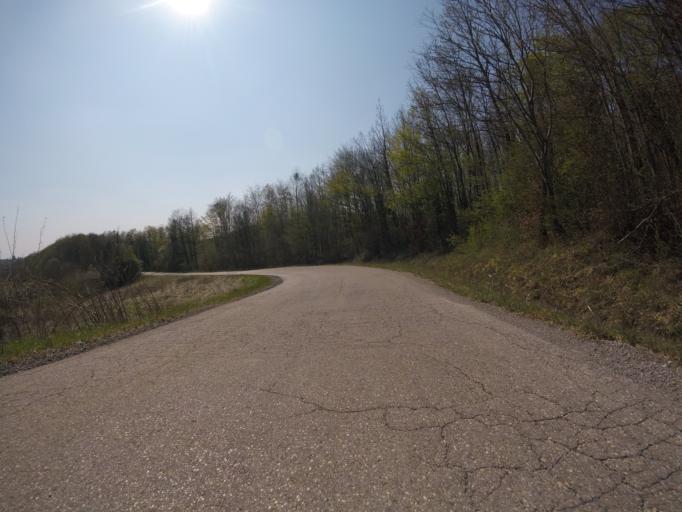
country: HR
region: Grad Zagreb
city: Strmec
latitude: 45.6230
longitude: 15.9522
